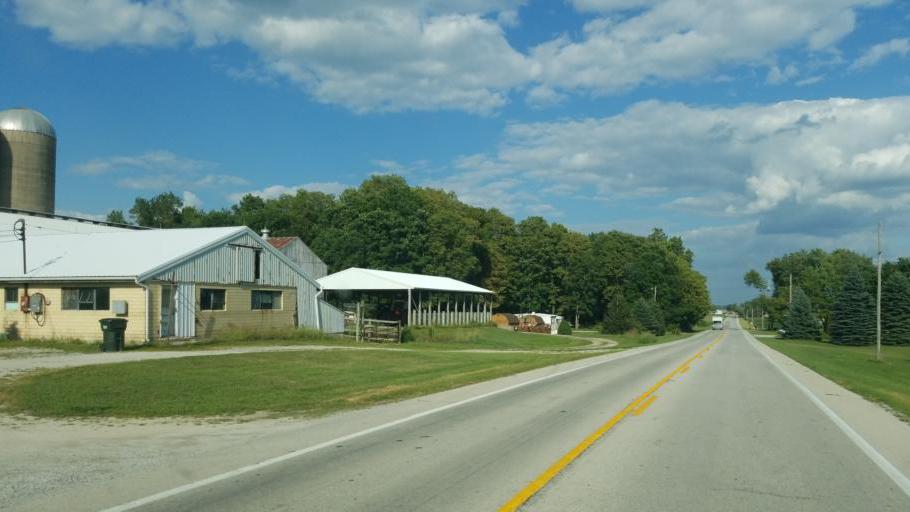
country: US
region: Ohio
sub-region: Wood County
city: Pemberville
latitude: 41.3553
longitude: -83.4864
